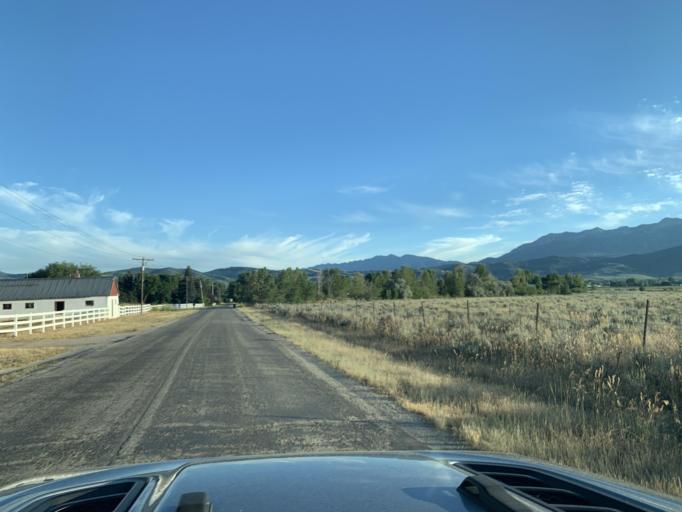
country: US
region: Utah
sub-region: Weber County
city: Wolf Creek
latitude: 41.2877
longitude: -111.7583
